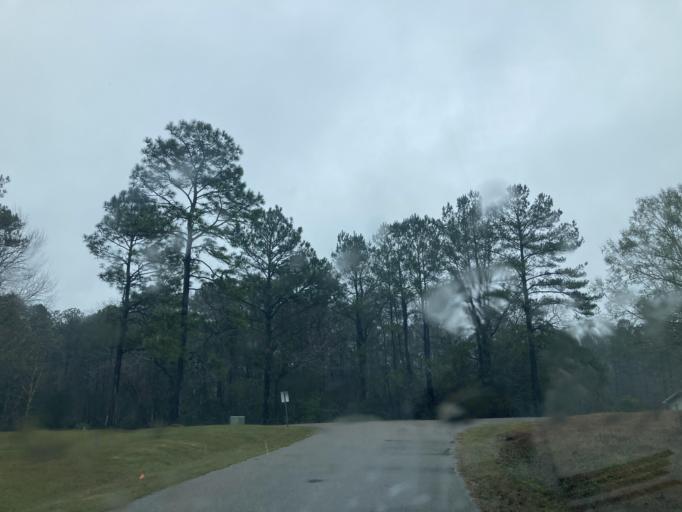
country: US
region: Mississippi
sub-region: Forrest County
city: Rawls Springs
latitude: 31.4952
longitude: -89.3620
